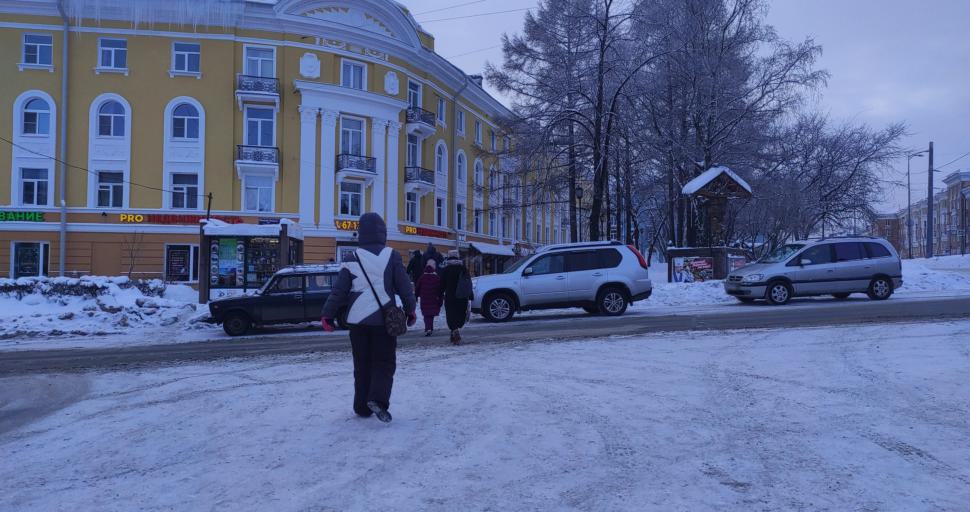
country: RU
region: Republic of Karelia
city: Petrozavodsk
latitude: 61.7888
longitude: 34.3600
